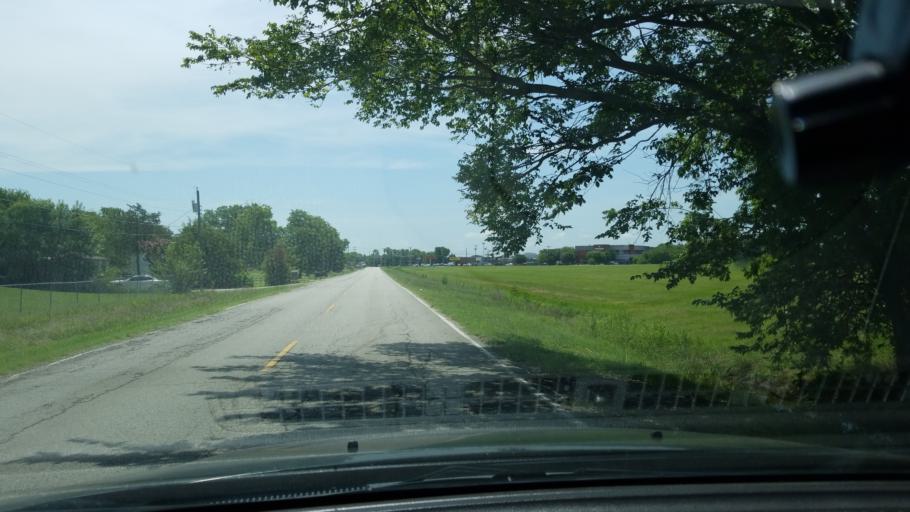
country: US
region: Texas
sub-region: Dallas County
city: Balch Springs
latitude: 32.7514
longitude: -96.6343
